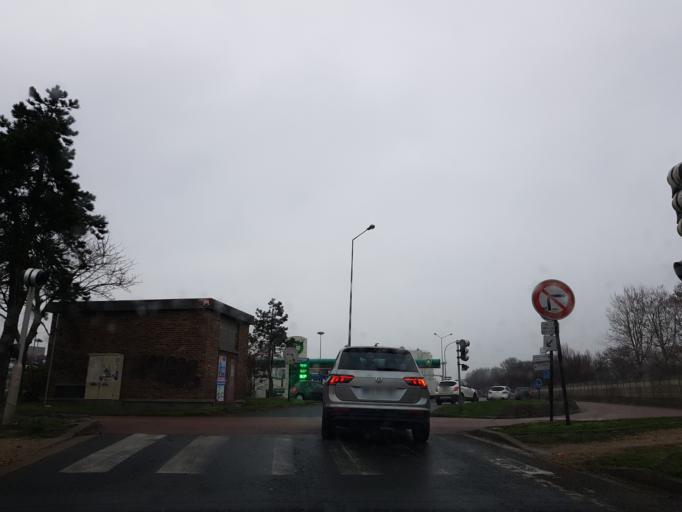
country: FR
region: Ile-de-France
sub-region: Departement du Val-de-Marne
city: Orly
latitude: 48.7543
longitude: 2.3754
